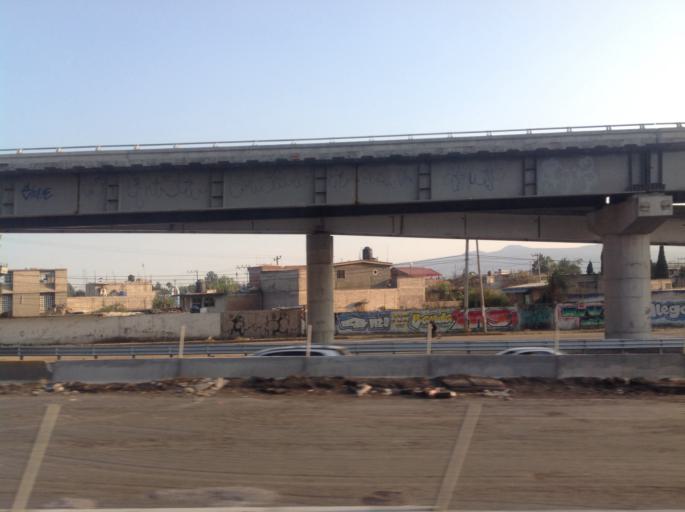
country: MX
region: Mexico
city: San Miguel Xico Viejo
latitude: 19.2907
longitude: -98.9164
